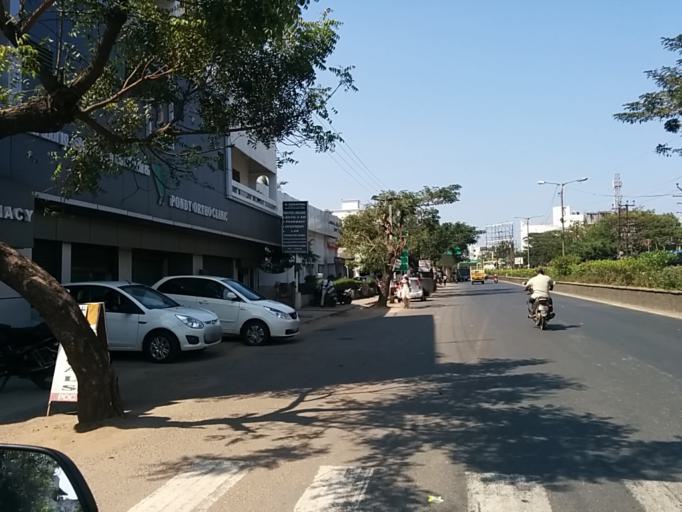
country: IN
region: Pondicherry
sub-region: Puducherry
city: Puducherry
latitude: 11.9395
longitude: 79.8080
